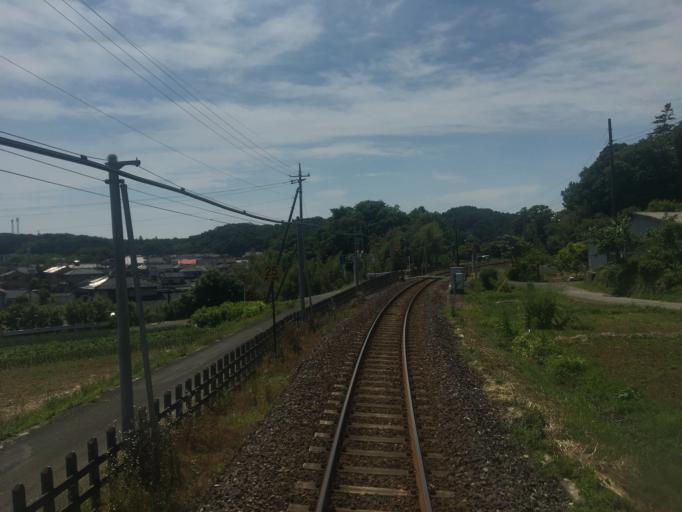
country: JP
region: Saitama
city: Ogawa
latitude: 36.0085
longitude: 139.2923
